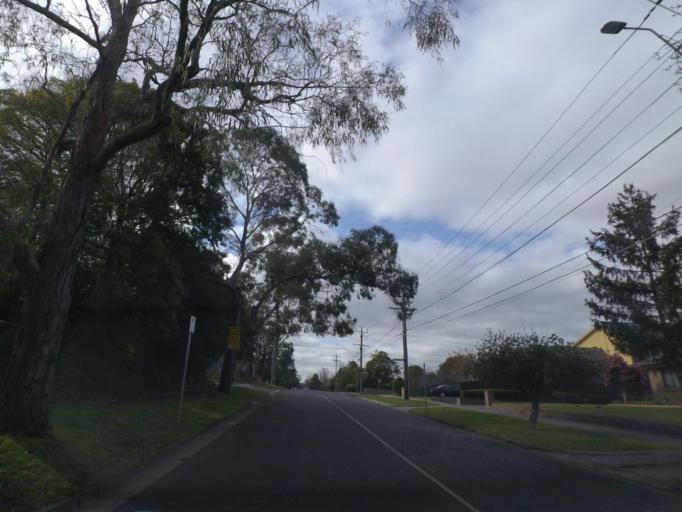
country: AU
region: Victoria
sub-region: Maroondah
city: Ringwood East
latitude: -37.8023
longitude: 145.2376
